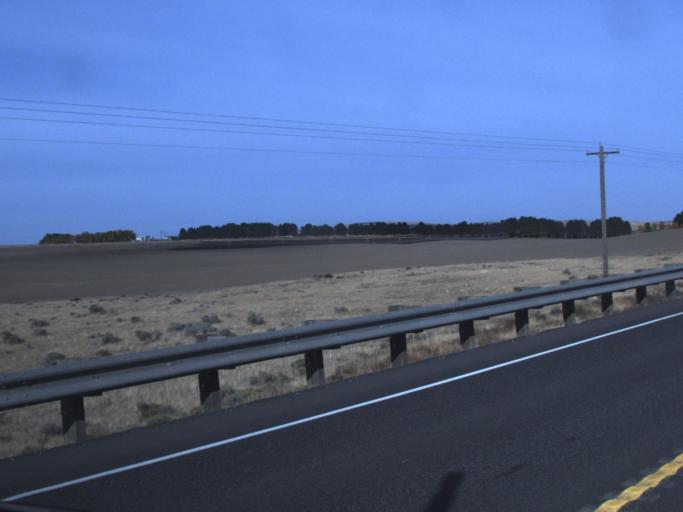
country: US
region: Oregon
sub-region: Morrow County
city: Irrigon
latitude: 45.9447
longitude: -119.5076
